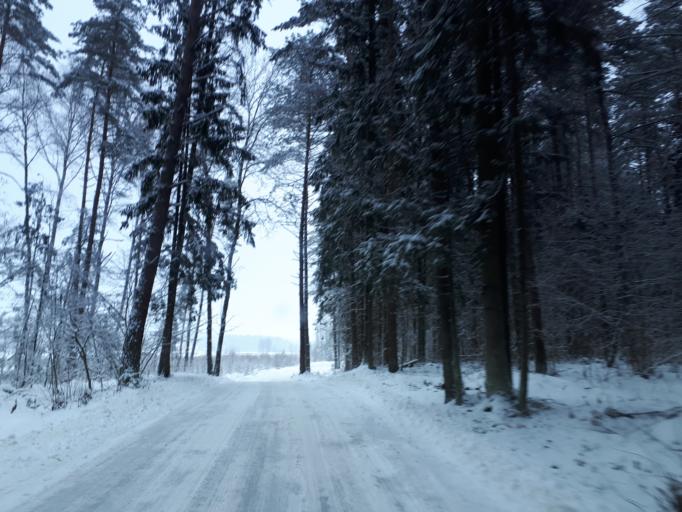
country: BY
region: Vitebsk
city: Vitebsk
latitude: 55.2636
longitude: 30.2134
